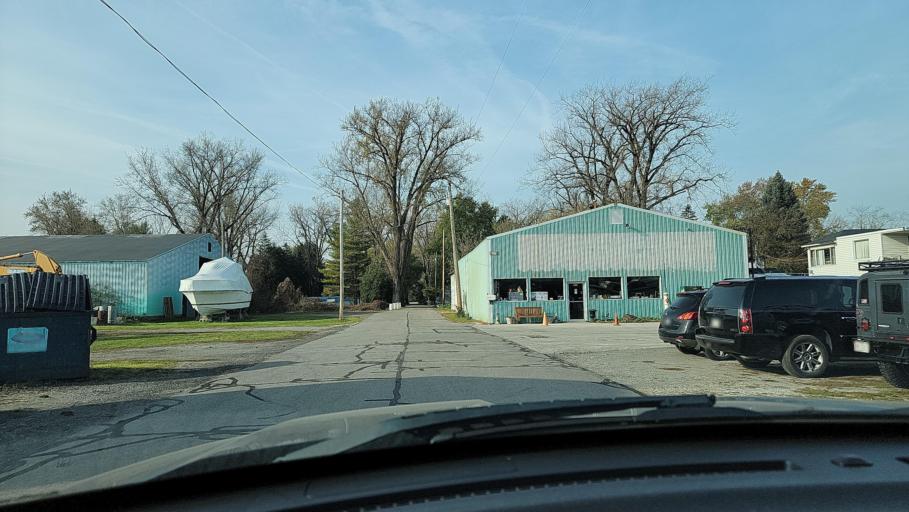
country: US
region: Indiana
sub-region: Porter County
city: Ogden Dunes
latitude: 41.6015
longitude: -87.1943
